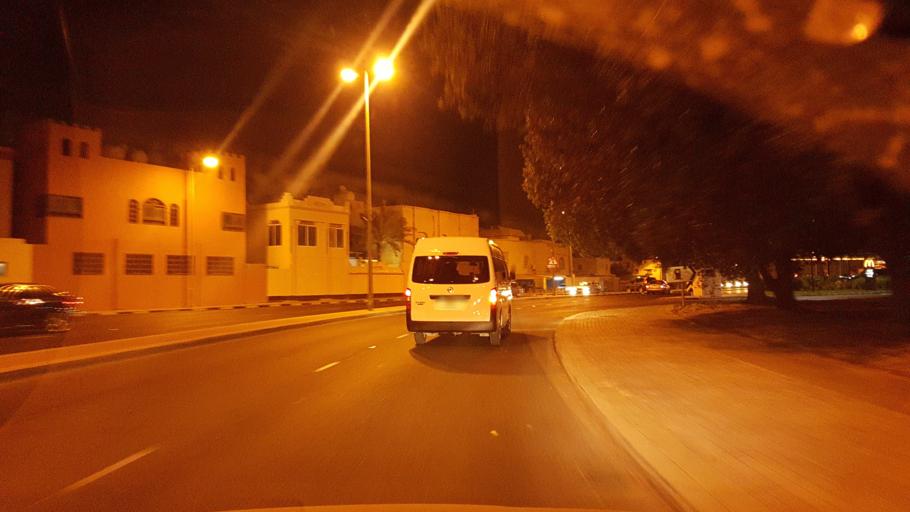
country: BH
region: Muharraq
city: Al Muharraq
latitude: 26.2592
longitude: 50.6295
